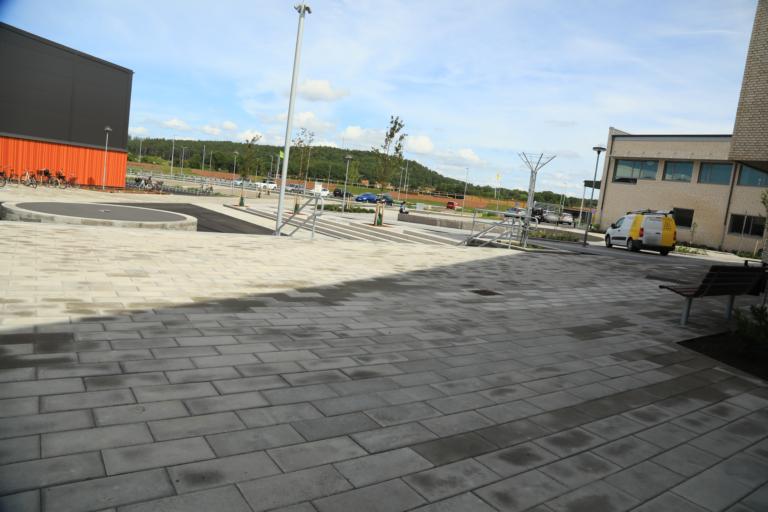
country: SE
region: Halland
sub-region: Varbergs Kommun
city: Varberg
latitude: 57.1377
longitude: 12.2763
